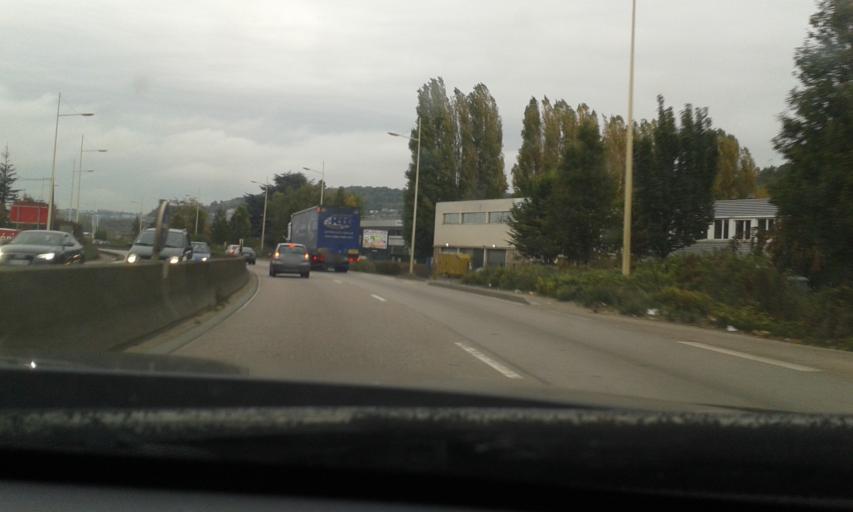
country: FR
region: Haute-Normandie
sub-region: Departement de la Seine-Maritime
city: Sotteville-les-Rouen
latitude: 49.4173
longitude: 1.1081
